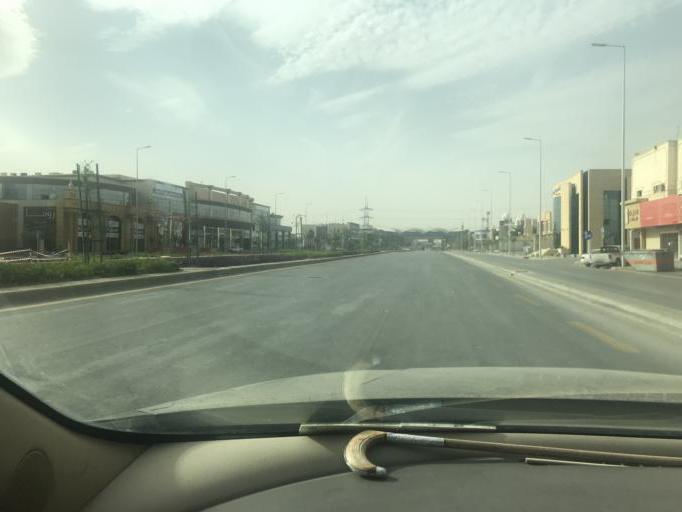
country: SA
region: Ar Riyad
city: Riyadh
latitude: 24.7803
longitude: 46.6635
